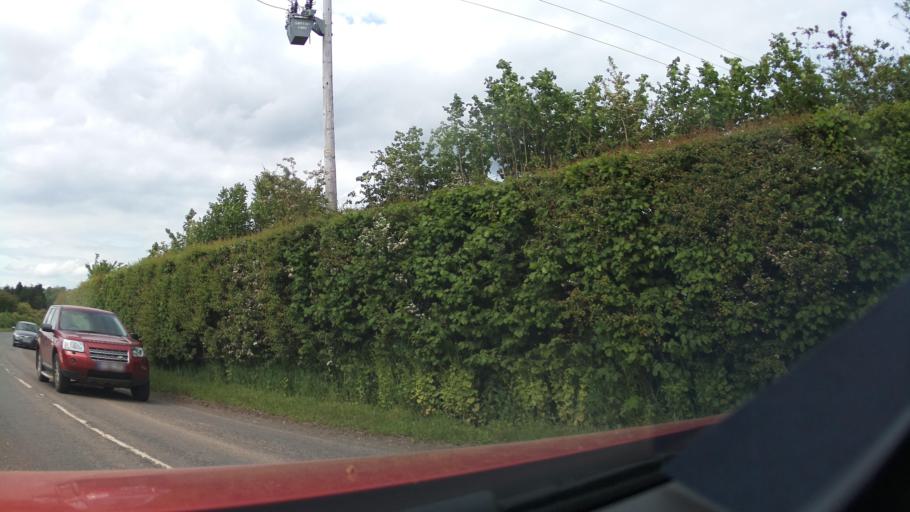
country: GB
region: England
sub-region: Herefordshire
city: Ledbury
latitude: 52.0636
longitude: -2.4454
